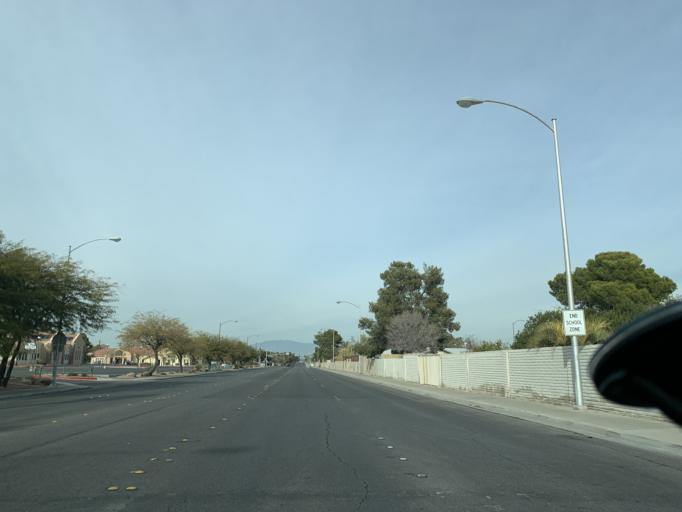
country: US
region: Nevada
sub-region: Clark County
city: Spring Valley
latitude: 36.0971
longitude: -115.2340
